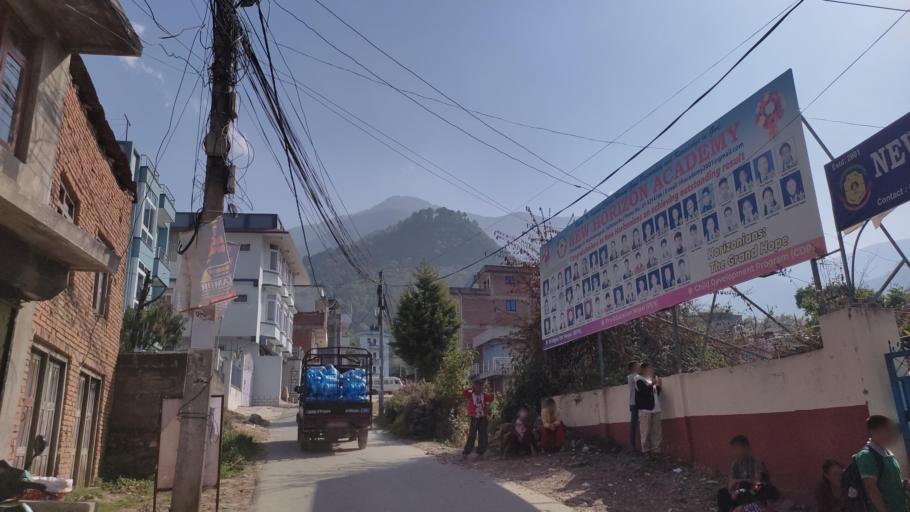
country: NP
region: Central Region
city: Kirtipur
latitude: 27.6717
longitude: 85.2507
